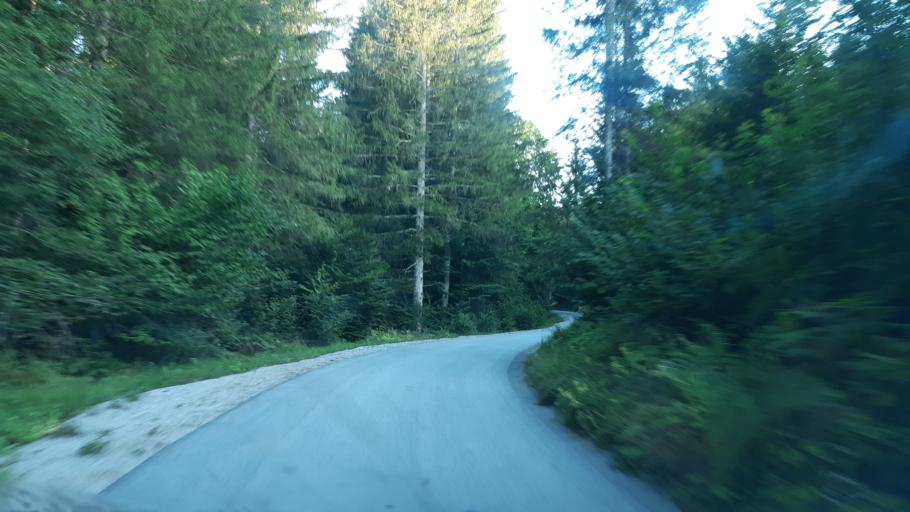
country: SI
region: Kocevje
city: Kocevje
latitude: 45.6636
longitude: 14.9140
